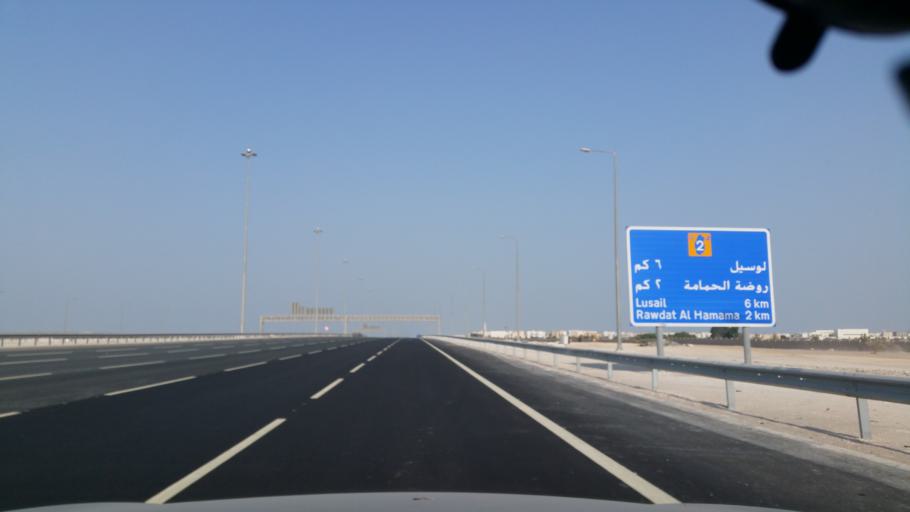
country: QA
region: Baladiyat Umm Salal
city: Umm Salal `Ali
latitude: 25.4515
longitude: 51.4234
